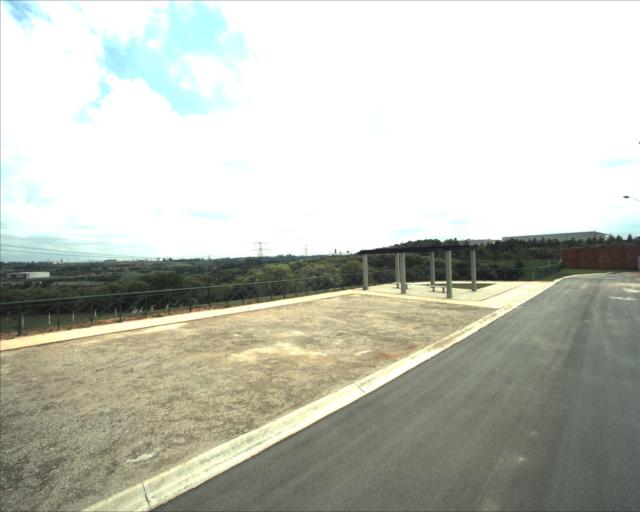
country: BR
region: Sao Paulo
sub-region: Sorocaba
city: Sorocaba
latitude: -23.4492
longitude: -47.3878
